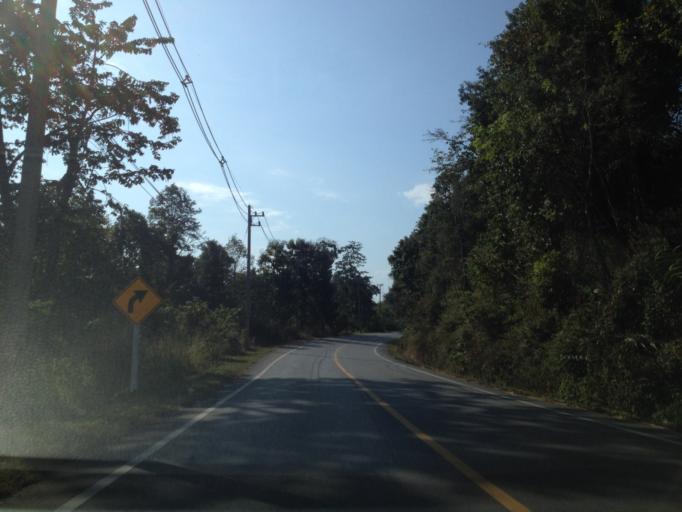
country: TH
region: Mae Hong Son
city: Pa Pae
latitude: 18.1597
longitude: 98.2343
